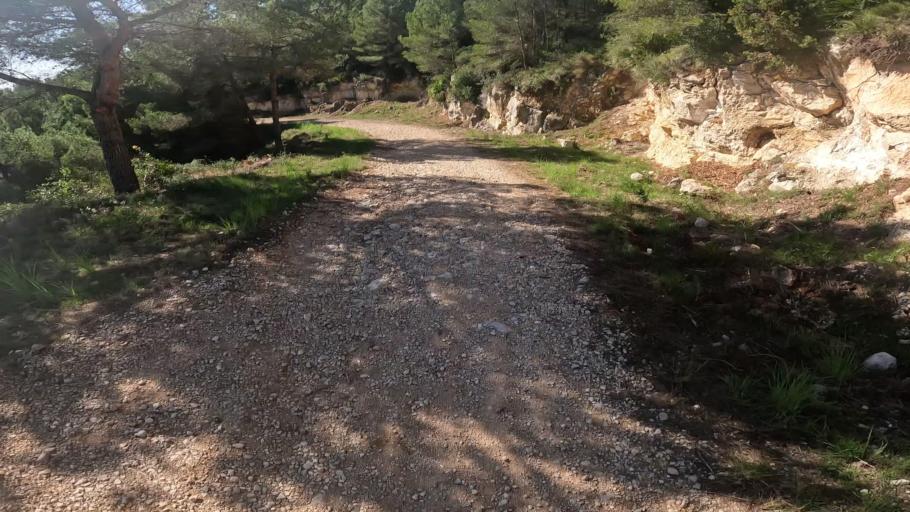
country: ES
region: Valencia
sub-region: Provincia de Castello
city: Alcoceber
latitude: 40.2671
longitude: 0.2720
